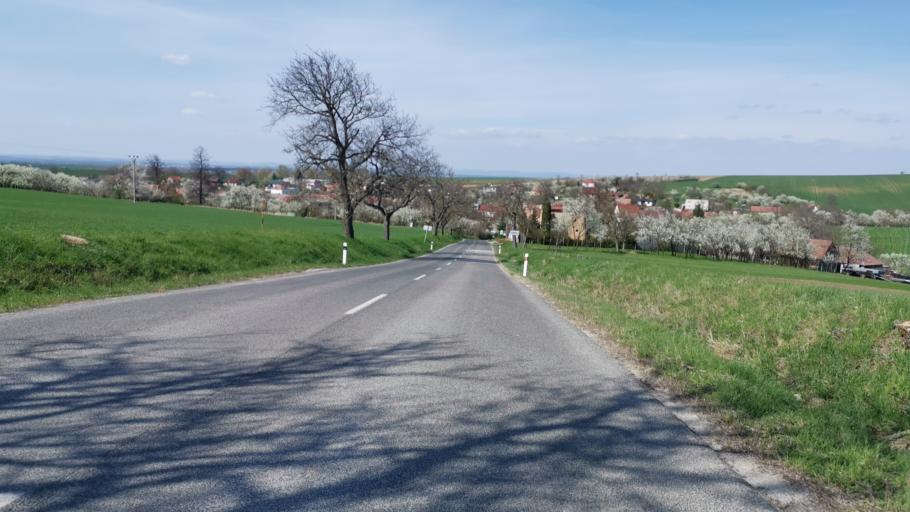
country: SK
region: Trnavsky
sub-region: Okres Skalica
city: Holic
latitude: 48.7461
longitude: 17.2019
